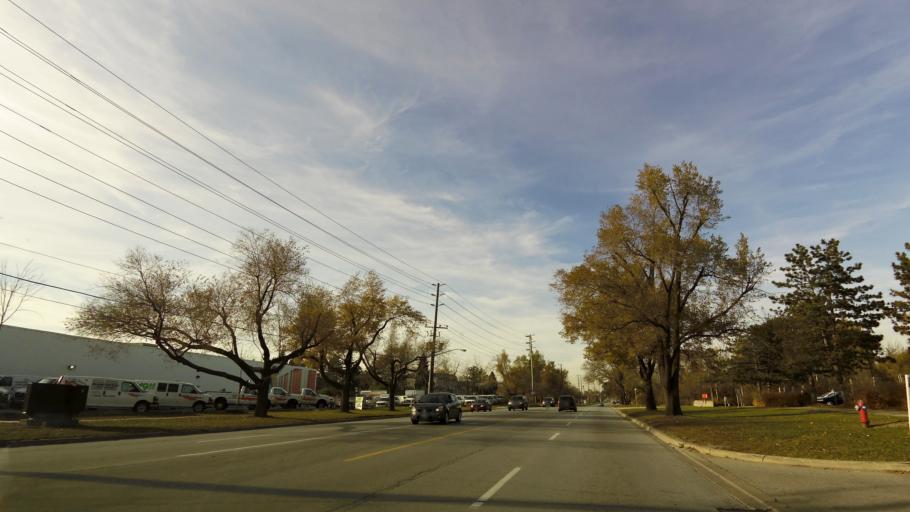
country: CA
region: Ontario
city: Brampton
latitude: 43.7175
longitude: -79.6843
